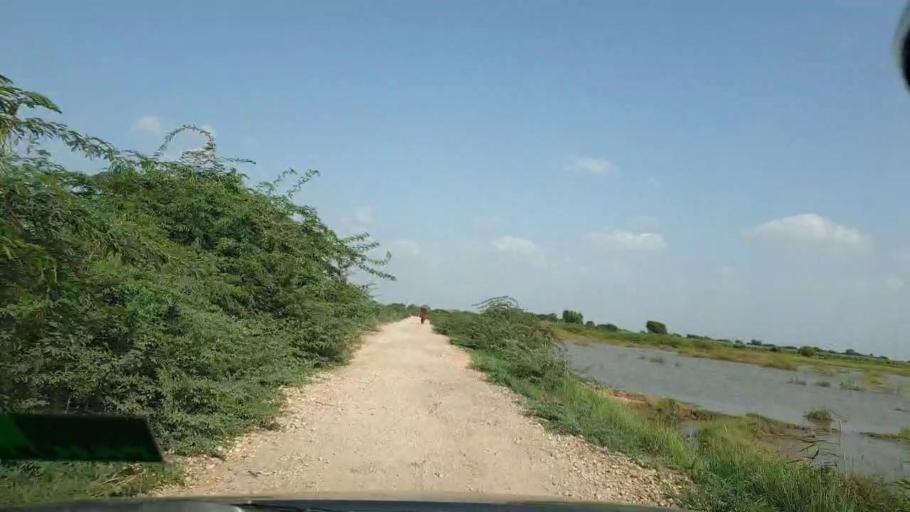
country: PK
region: Sindh
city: Tando Bago
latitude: 24.6827
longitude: 69.1954
